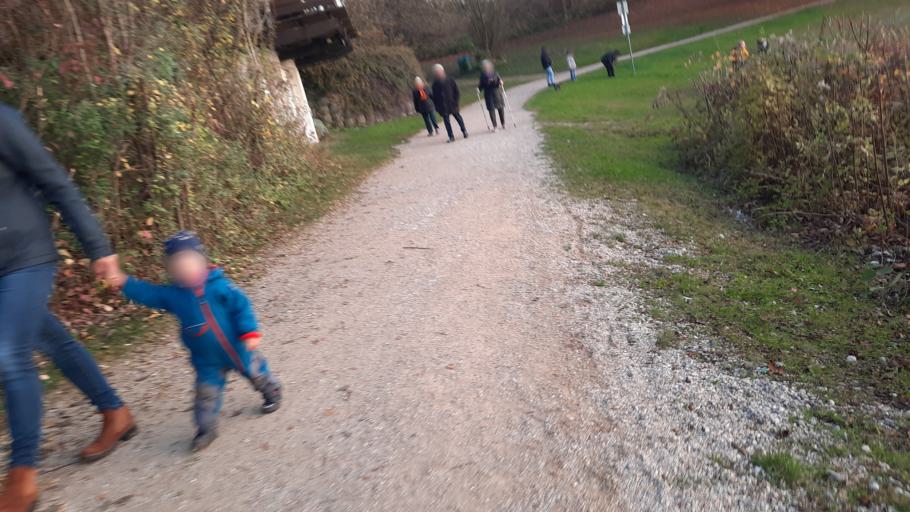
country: DE
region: Bavaria
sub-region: Upper Bavaria
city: Feldkirchen
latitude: 48.1552
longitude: 11.7420
